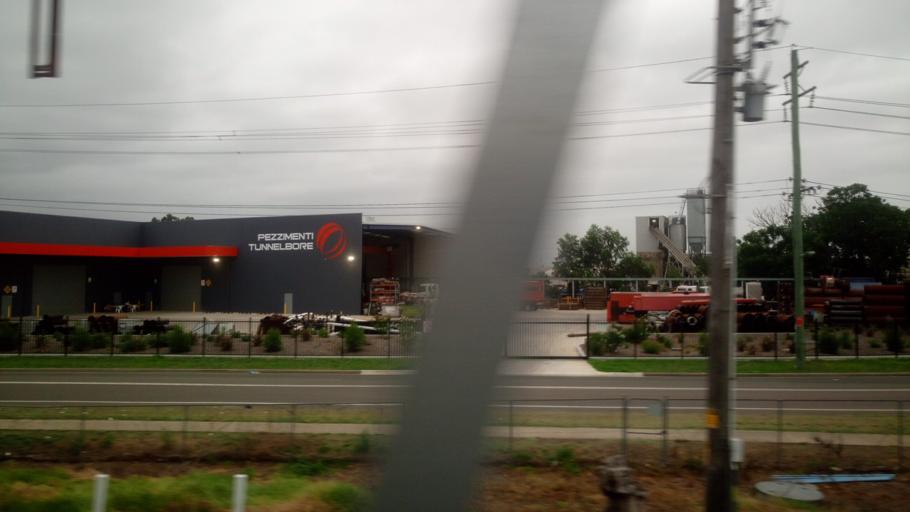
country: AU
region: New South Wales
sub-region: Penrith Municipality
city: Penrith
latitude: -33.7452
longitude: 150.6741
